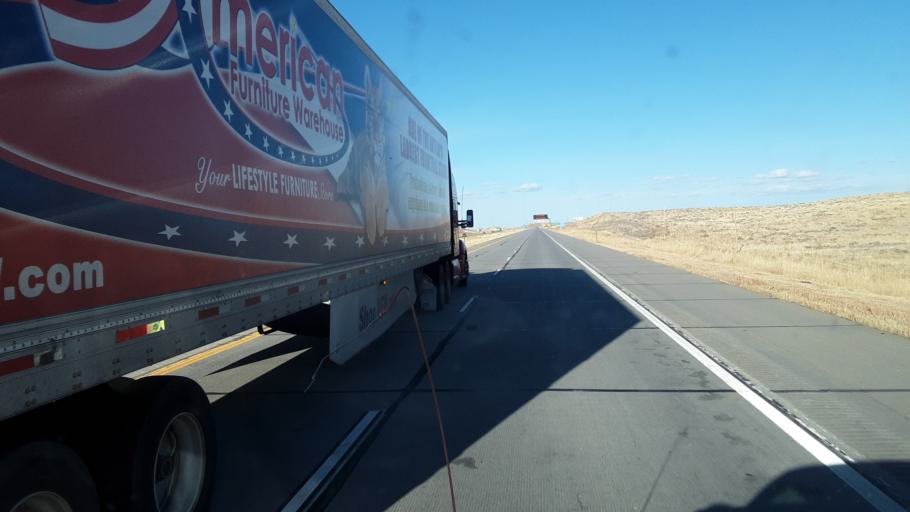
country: US
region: Colorado
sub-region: Logan County
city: Sterling
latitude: 40.6049
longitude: -103.1812
